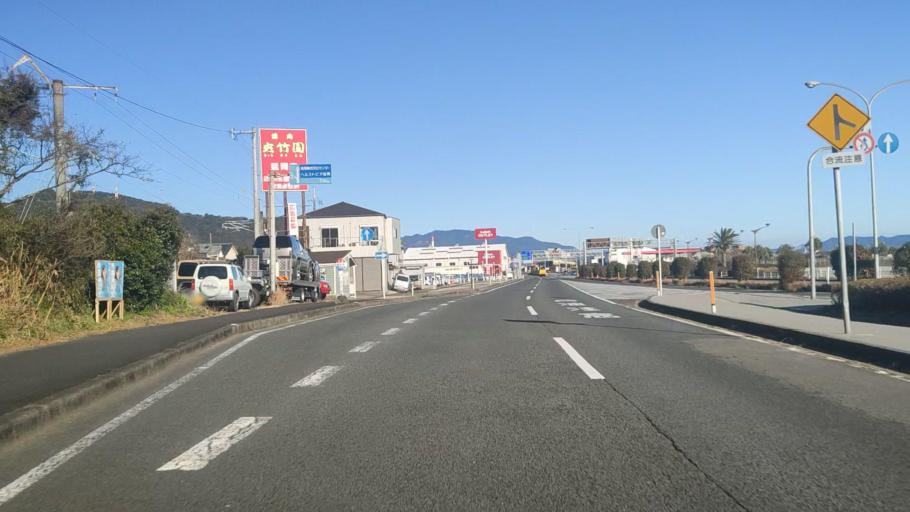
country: JP
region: Miyazaki
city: Nobeoka
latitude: 32.5404
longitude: 131.6784
